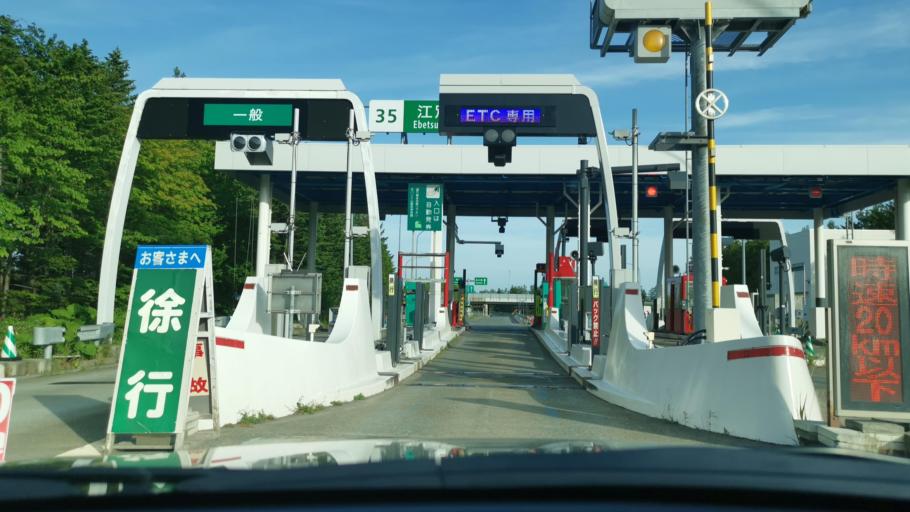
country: JP
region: Hokkaido
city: Ebetsu
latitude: 43.1068
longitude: 141.5982
